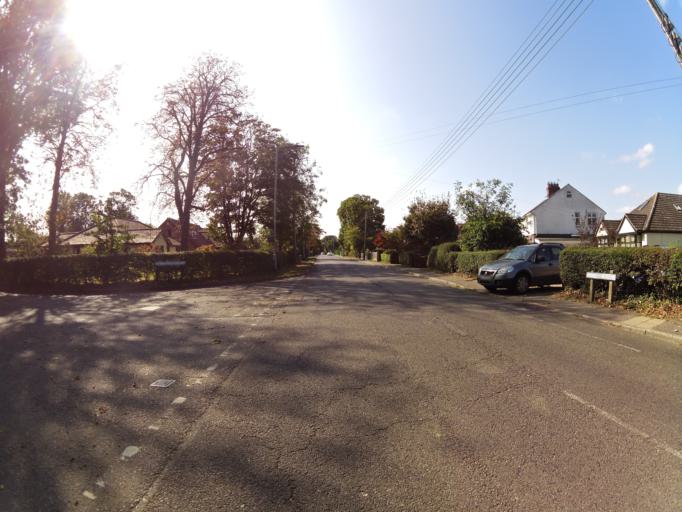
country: GB
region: England
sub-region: Suffolk
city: Kessingland
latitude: 52.4627
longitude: 1.7077
